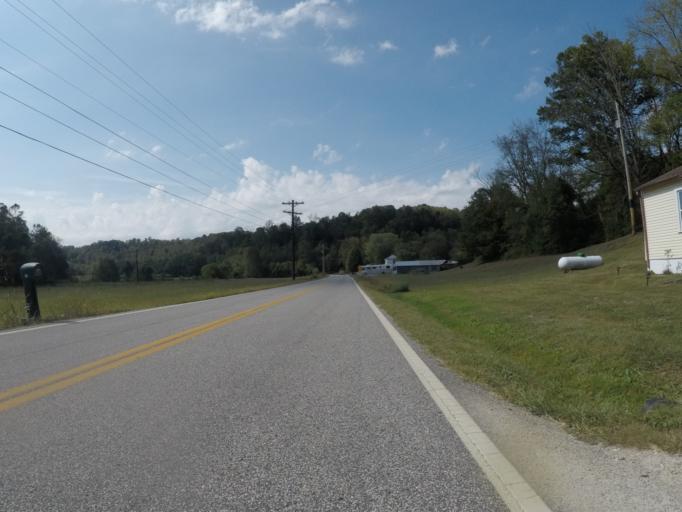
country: US
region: West Virginia
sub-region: Cabell County
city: Lesage
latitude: 38.5390
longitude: -82.3929
